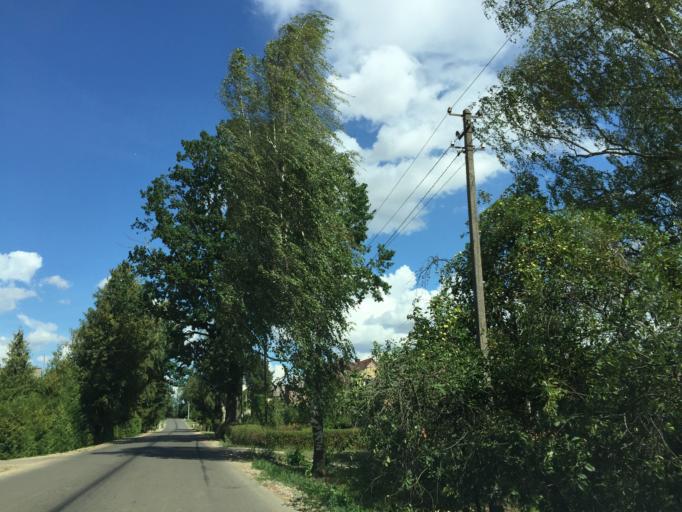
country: LV
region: Rundales
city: Pilsrundale
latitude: 56.3139
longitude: 23.9108
